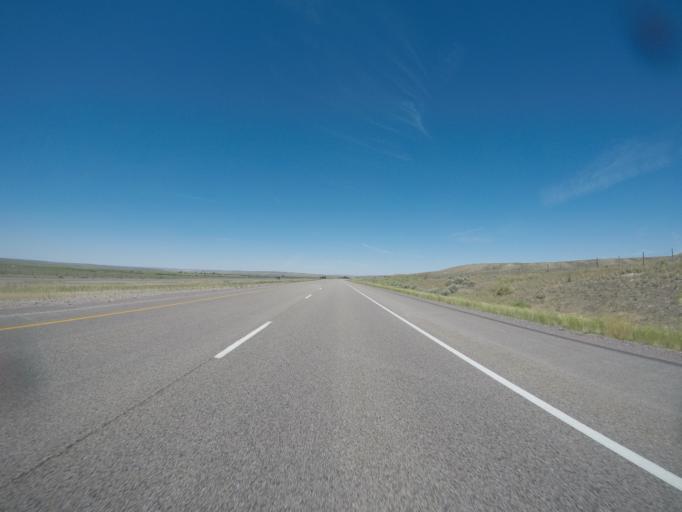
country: US
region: Wyoming
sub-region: Carbon County
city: Saratoga
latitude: 41.7359
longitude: -106.7410
